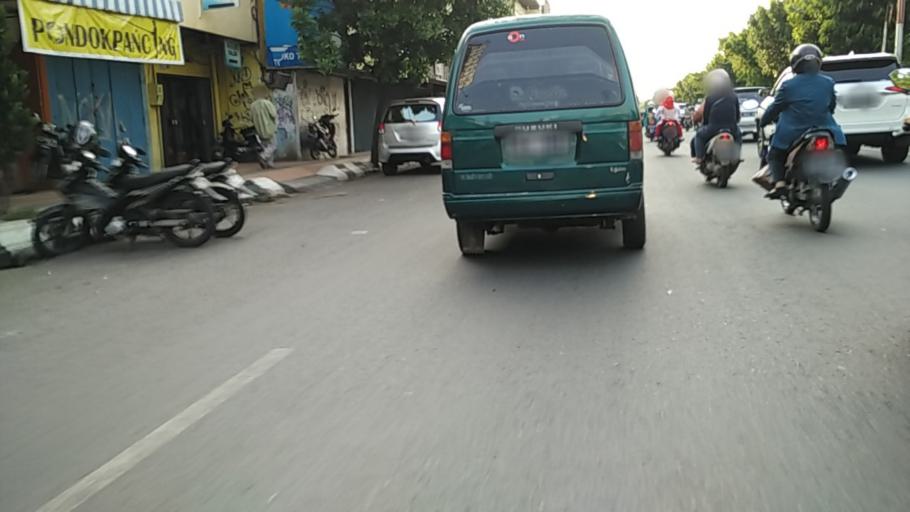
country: ID
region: Central Java
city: Semarang
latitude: -6.9835
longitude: 110.4071
